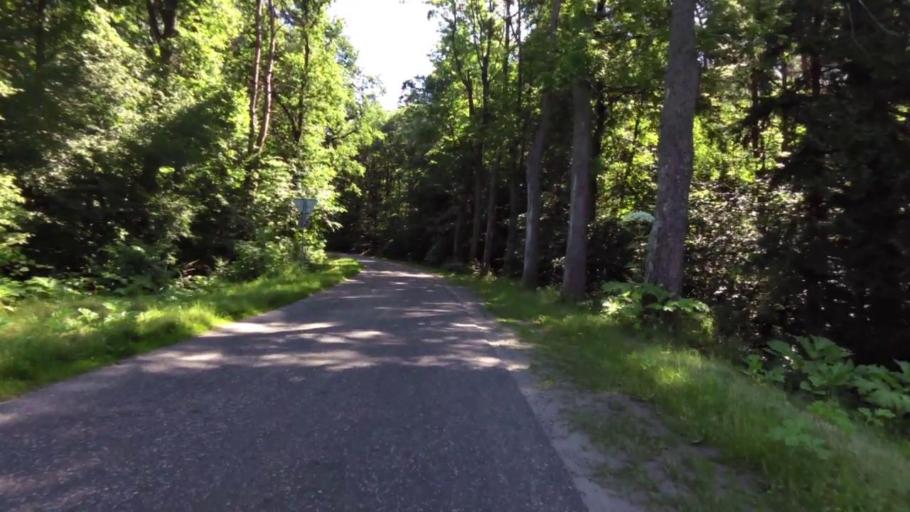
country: PL
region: West Pomeranian Voivodeship
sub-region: Powiat bialogardzki
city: Bialogard
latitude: 53.9411
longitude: 15.9607
